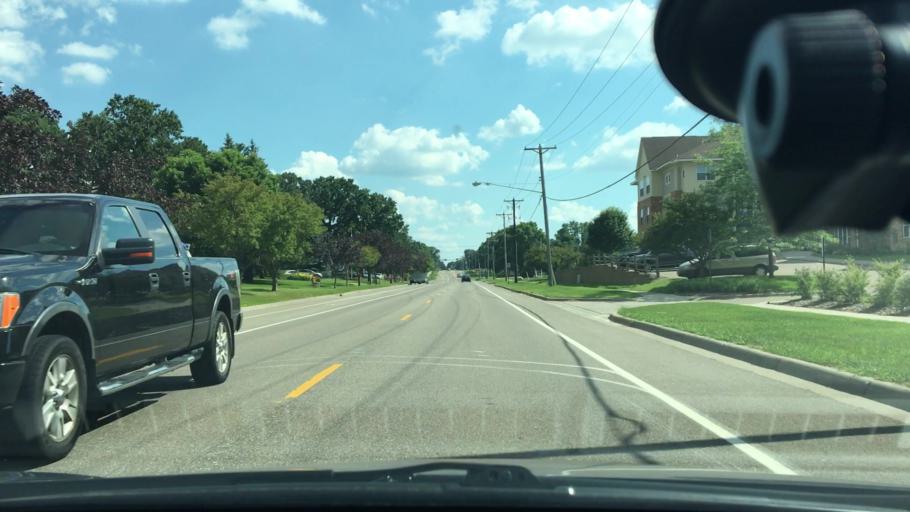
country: US
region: Minnesota
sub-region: Hennepin County
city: New Hope
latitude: 45.0535
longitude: -93.3907
